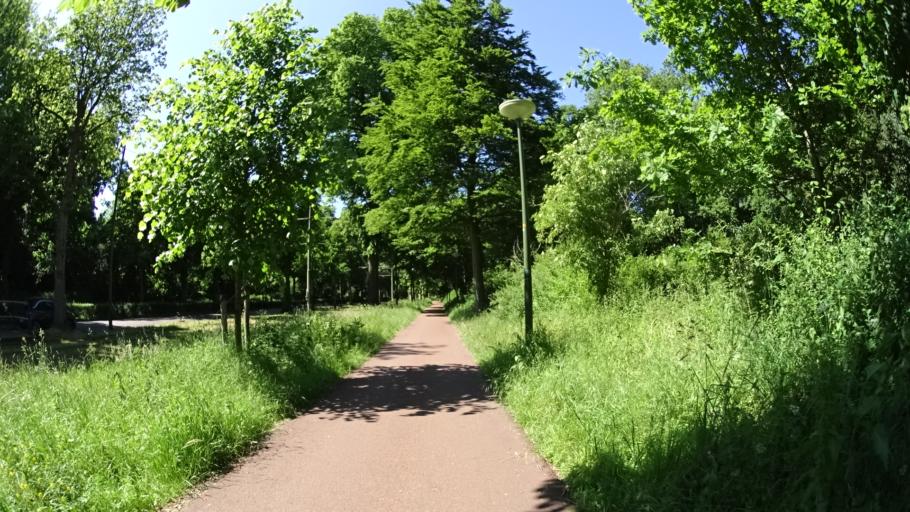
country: NL
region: South Holland
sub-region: Gemeente Den Haag
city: The Hague
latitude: 52.0900
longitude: 4.2938
